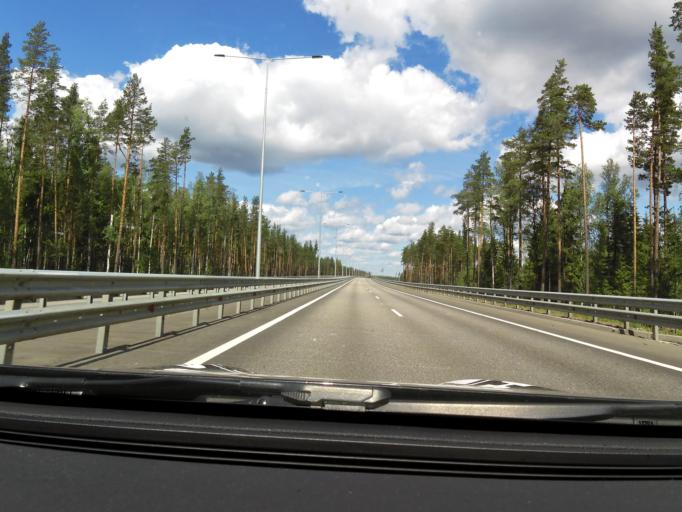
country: RU
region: Tverskaya
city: Krasnomayskiy
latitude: 57.5080
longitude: 34.2894
